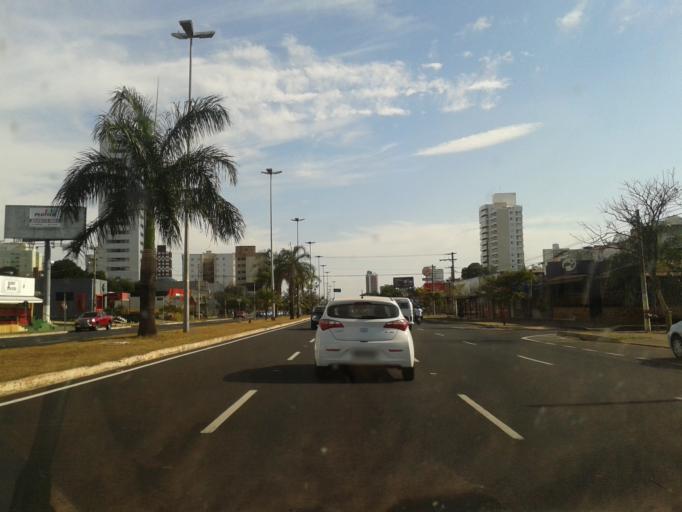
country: BR
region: Minas Gerais
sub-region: Uberlandia
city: Uberlandia
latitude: -18.9157
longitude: -48.2637
